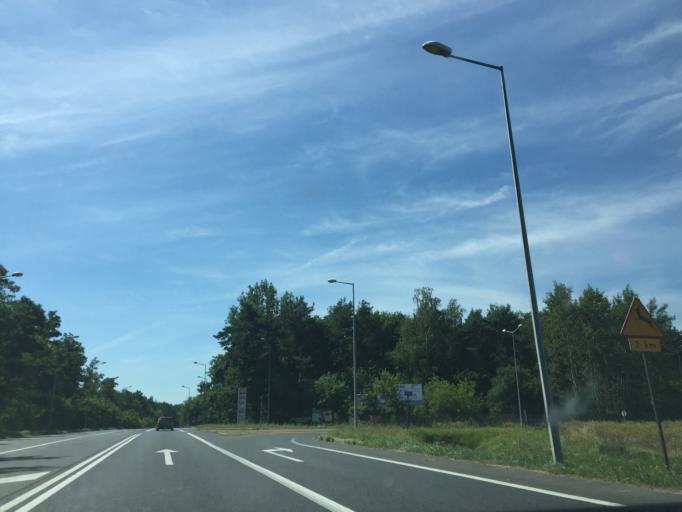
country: PL
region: Lodz Voivodeship
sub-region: Piotrkow Trybunalski
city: Piotrkow Trybunalski
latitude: 51.4384
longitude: 19.7208
